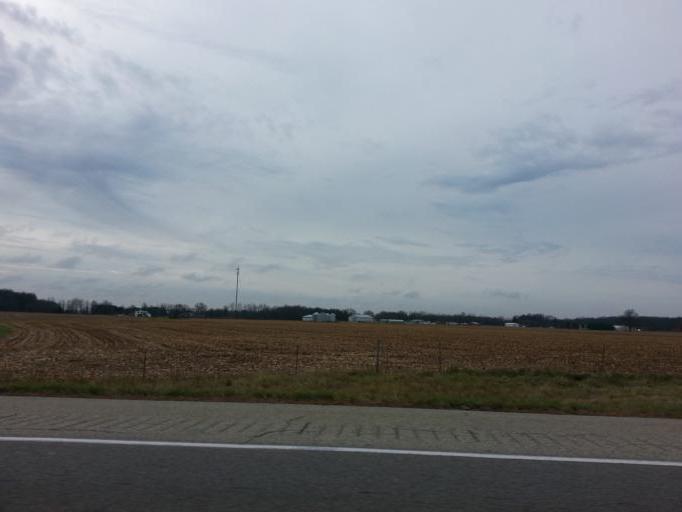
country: US
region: Indiana
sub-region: Decatur County
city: Greensburg
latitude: 39.3235
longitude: -85.3780
